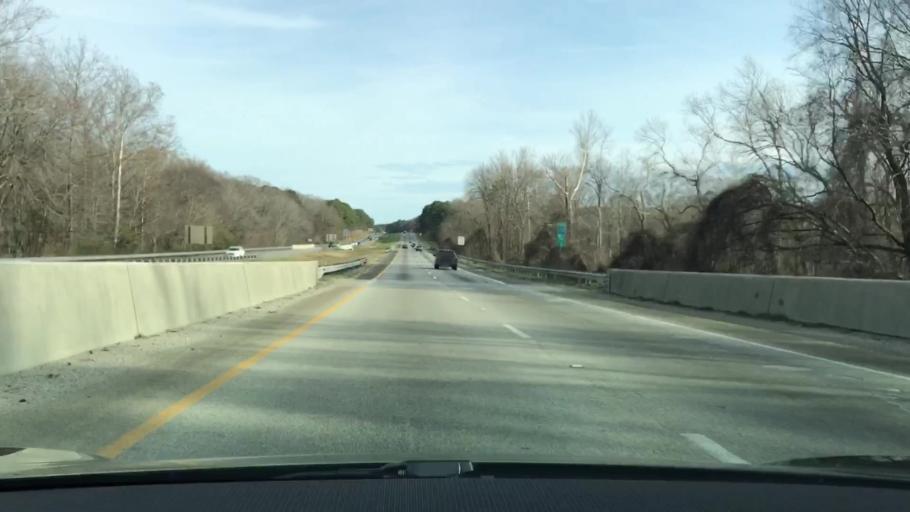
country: US
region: Georgia
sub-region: Newton County
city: Covington
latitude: 33.6109
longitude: -83.8068
